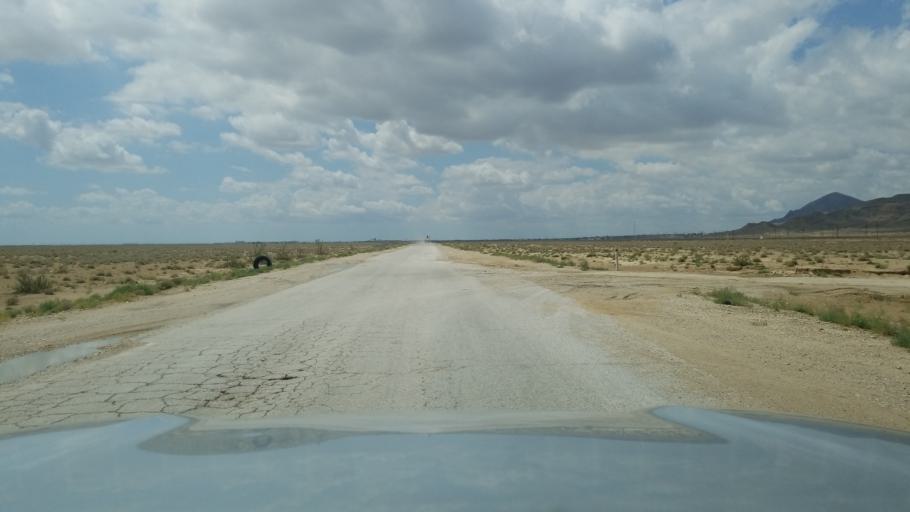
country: TM
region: Balkan
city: Balkanabat
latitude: 39.4819
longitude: 54.4456
